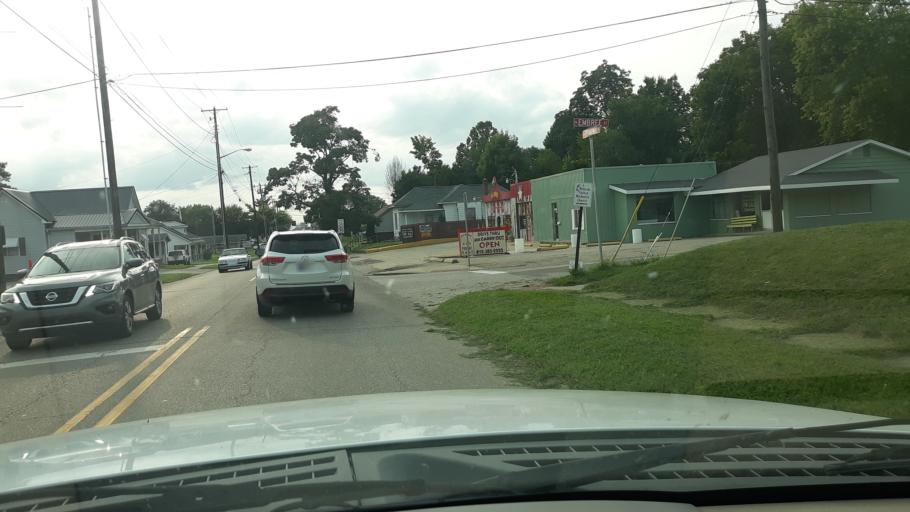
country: US
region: Indiana
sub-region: Gibson County
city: Princeton
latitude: 38.3554
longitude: -87.5756
